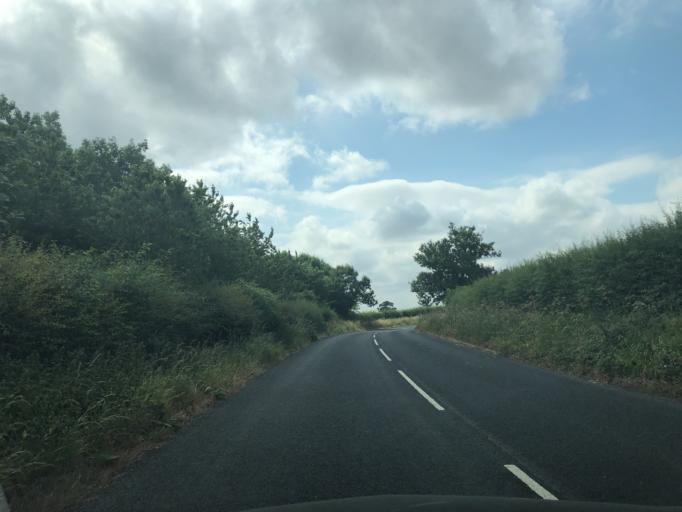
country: GB
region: England
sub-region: North Yorkshire
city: Stokesley
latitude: 54.4612
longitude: -1.2324
